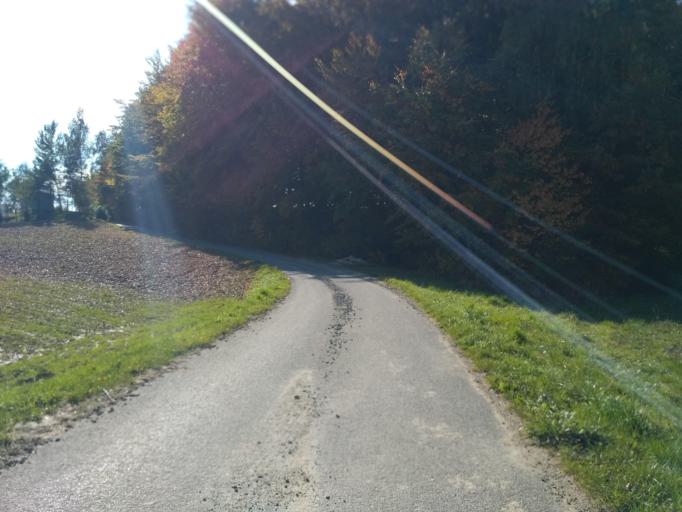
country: PL
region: Subcarpathian Voivodeship
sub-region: Powiat debicki
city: Slotowa
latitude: 49.9363
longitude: 21.2770
